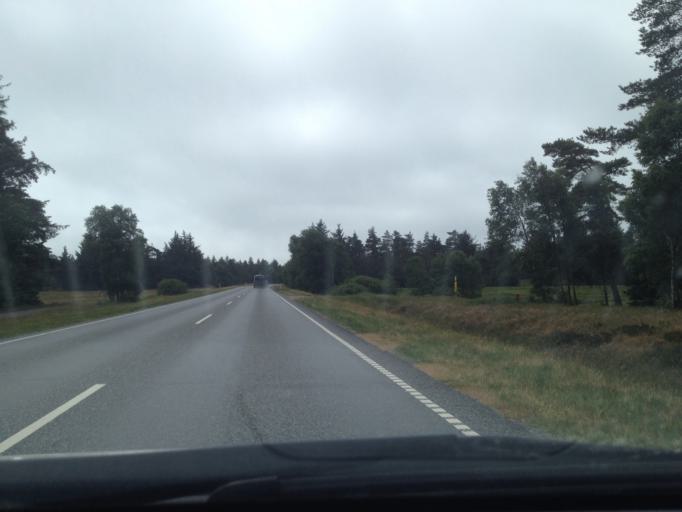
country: DK
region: South Denmark
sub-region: Varde Kommune
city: Oksbol
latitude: 55.5840
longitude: 8.2297
